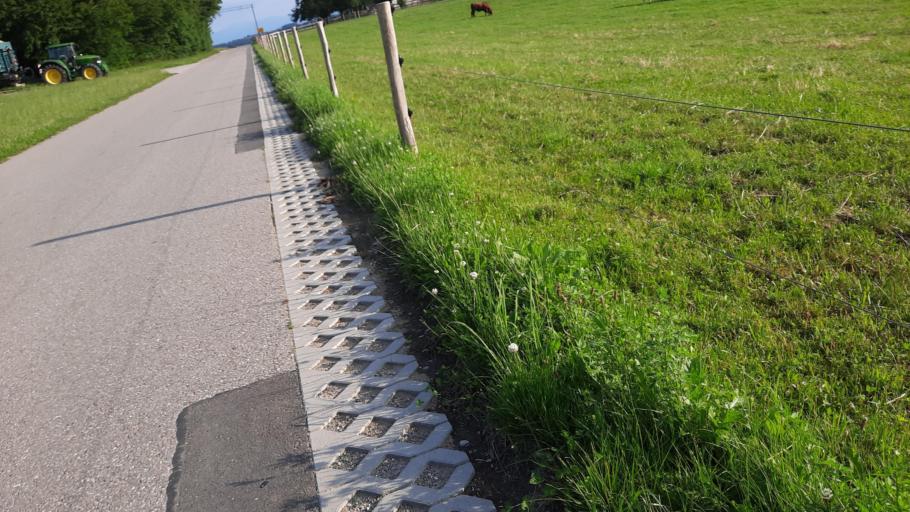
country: DE
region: Bavaria
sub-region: Upper Bavaria
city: Glonn
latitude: 47.9615
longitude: 11.8989
